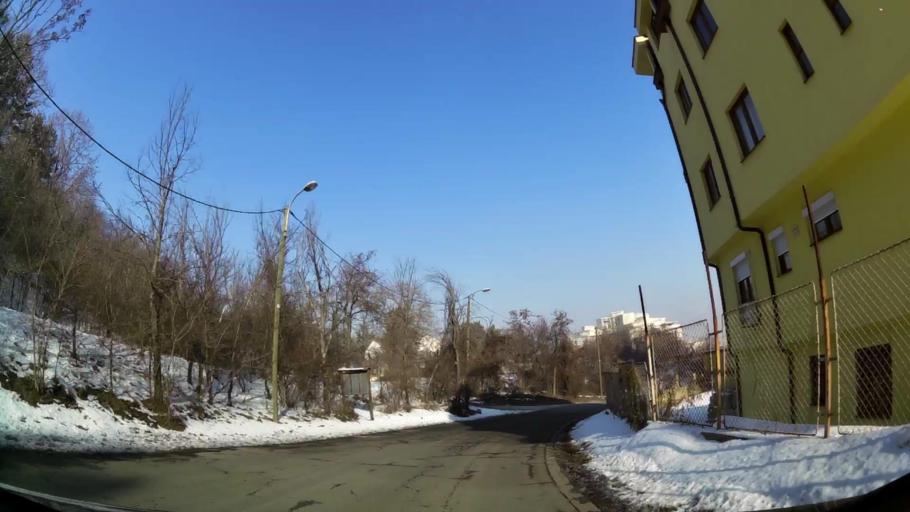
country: MK
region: Karpos
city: Skopje
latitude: 41.9814
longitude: 21.4209
